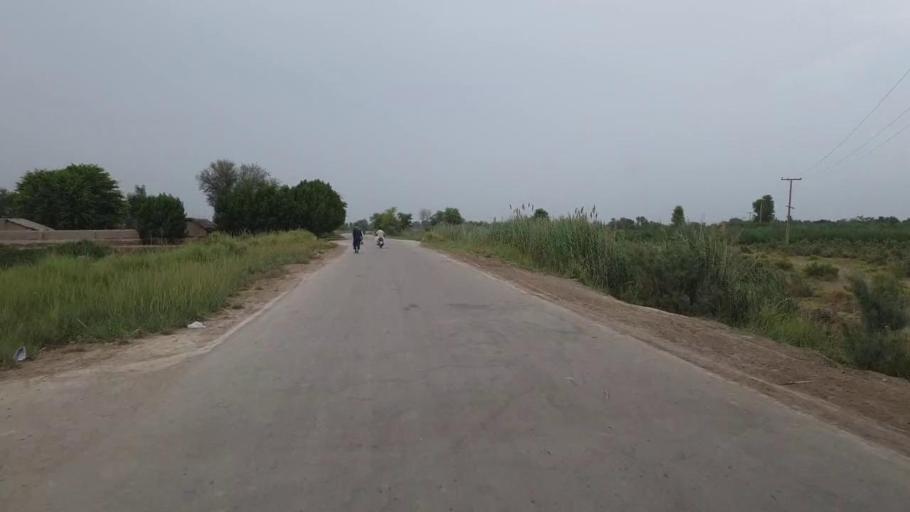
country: PK
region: Sindh
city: Bandhi
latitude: 26.5393
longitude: 68.2195
